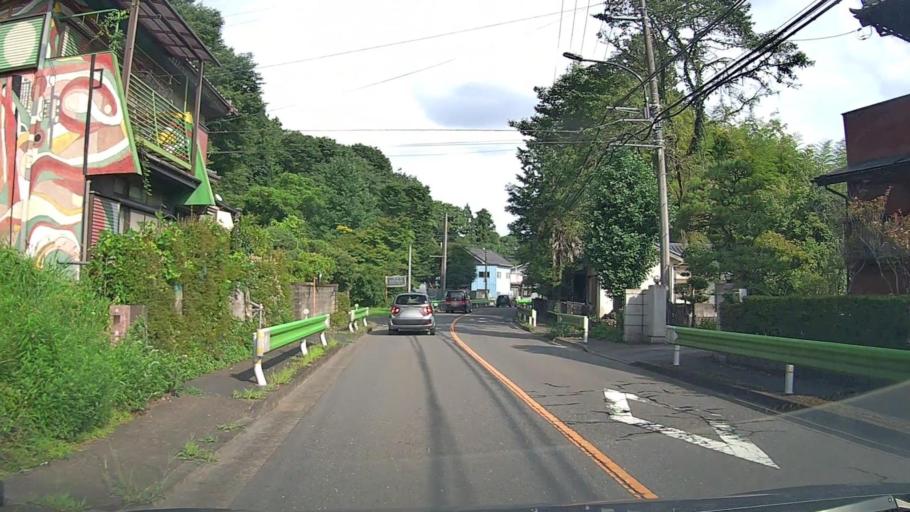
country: JP
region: Tokyo
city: Itsukaichi
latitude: 35.7088
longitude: 139.2419
